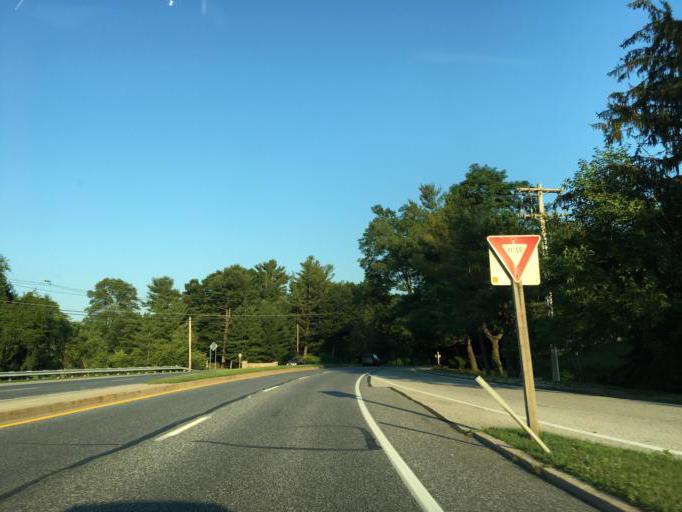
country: US
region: Maryland
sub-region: Baltimore County
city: Lutherville
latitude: 39.4024
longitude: -76.6304
